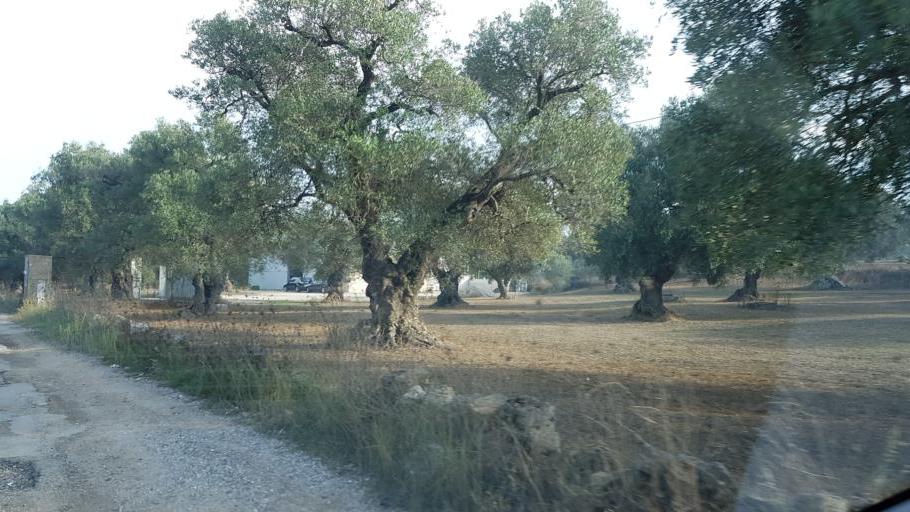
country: IT
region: Apulia
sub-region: Provincia di Brindisi
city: Oria
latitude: 40.4992
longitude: 17.6582
